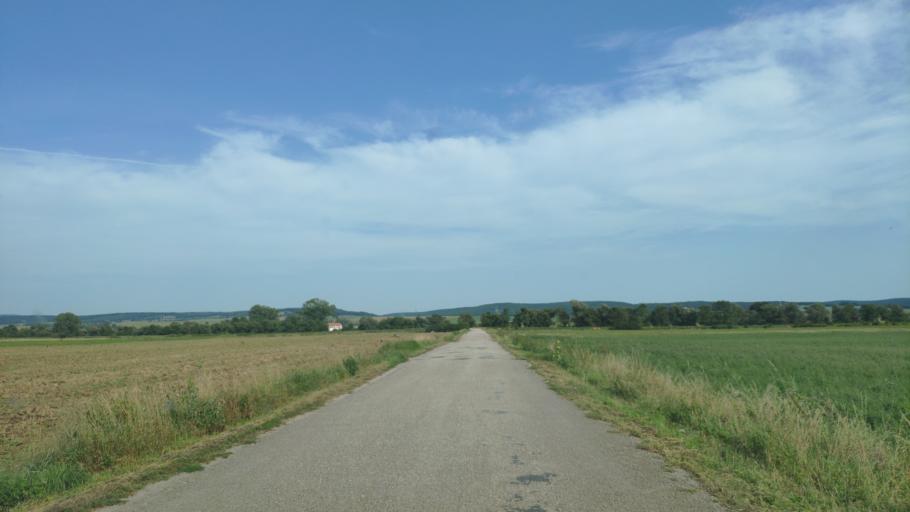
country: HU
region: Borsod-Abauj-Zemplen
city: Putnok
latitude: 48.4543
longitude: 20.3266
